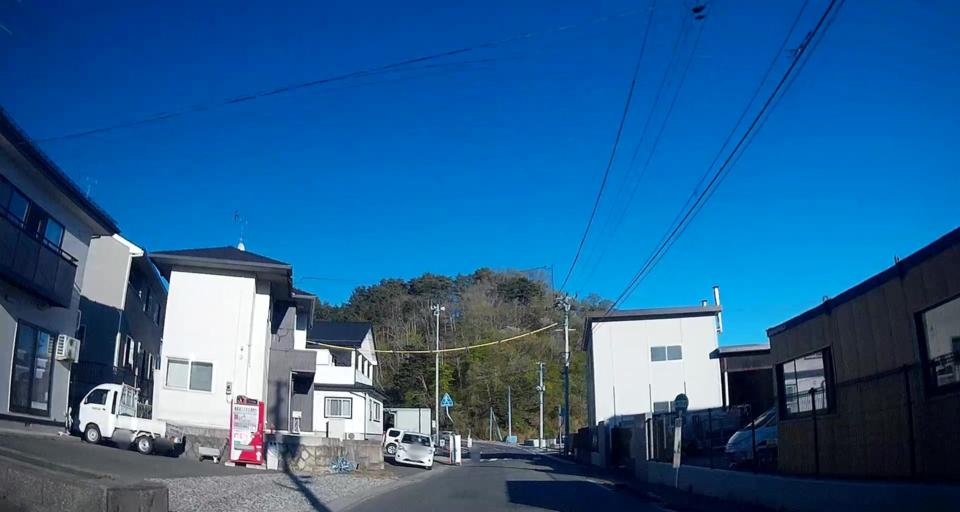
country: JP
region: Iwate
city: Miyako
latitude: 39.6452
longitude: 141.9742
